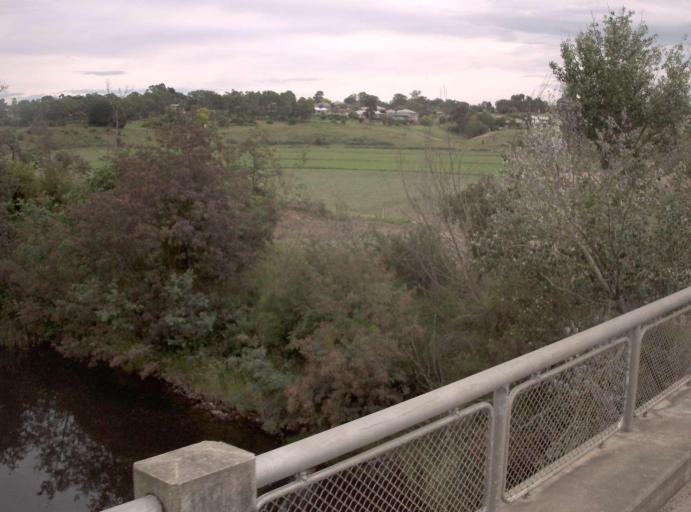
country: AU
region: Victoria
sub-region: East Gippsland
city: Bairnsdale
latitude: -37.8142
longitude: 147.6178
